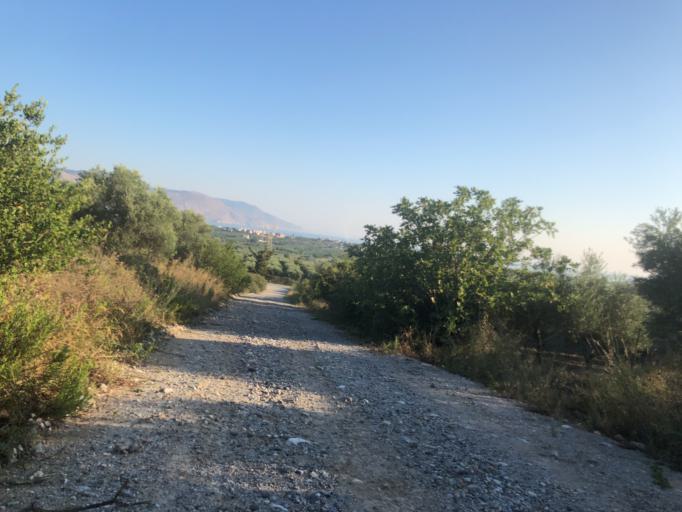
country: GR
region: Crete
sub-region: Nomos Chanias
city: Georgioupolis
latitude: 35.3373
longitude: 24.2900
